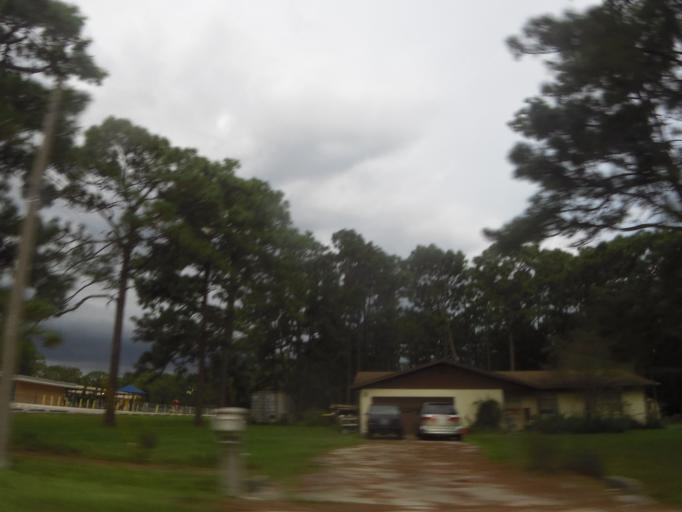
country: US
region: Florida
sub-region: Clay County
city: Bellair-Meadowbrook Terrace
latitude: 30.2843
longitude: -81.7871
